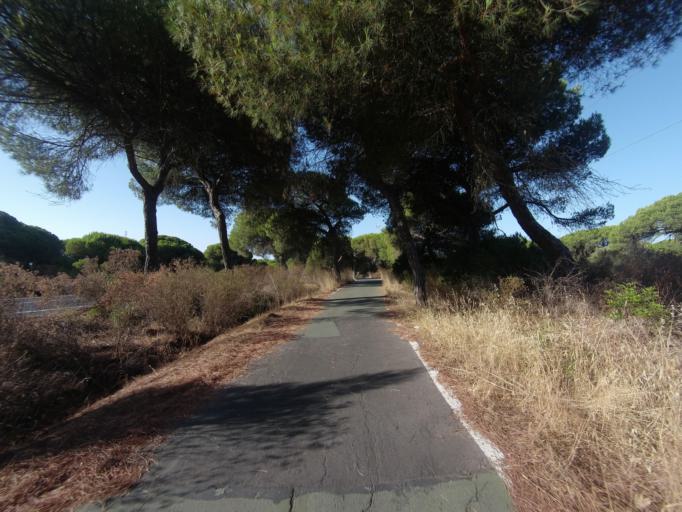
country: ES
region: Andalusia
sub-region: Provincia de Huelva
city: Aljaraque
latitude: 37.2120
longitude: -7.0272
